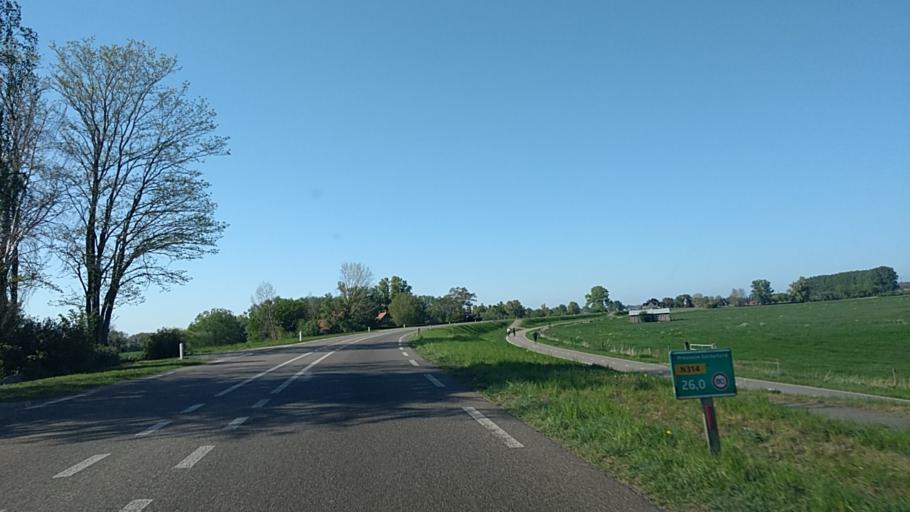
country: NL
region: Gelderland
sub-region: Gemeente Bronckhorst
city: Baak
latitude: 52.0910
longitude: 6.2198
